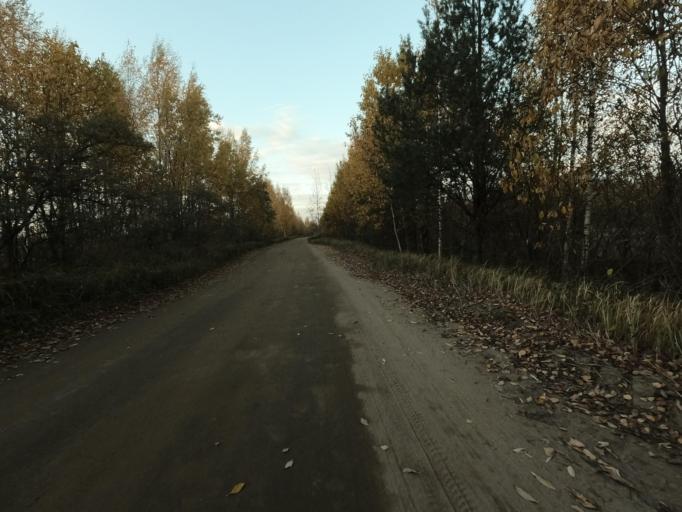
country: RU
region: Leningrad
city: Mga
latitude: 59.7959
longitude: 31.2004
